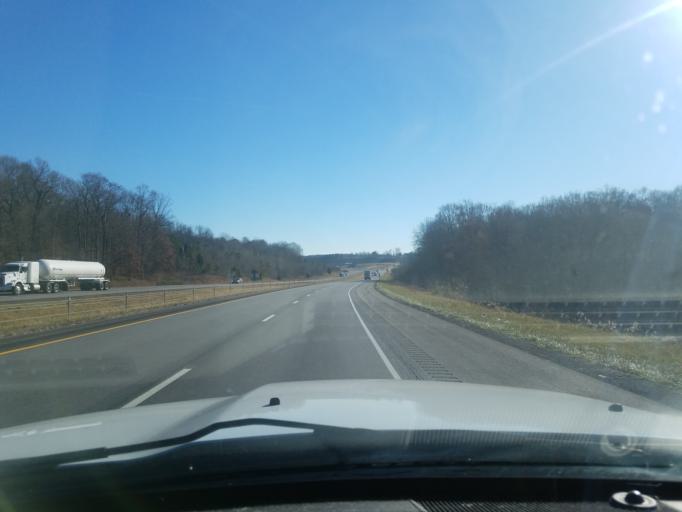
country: US
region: Indiana
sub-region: Crawford County
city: English
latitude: 38.2293
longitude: -86.6047
